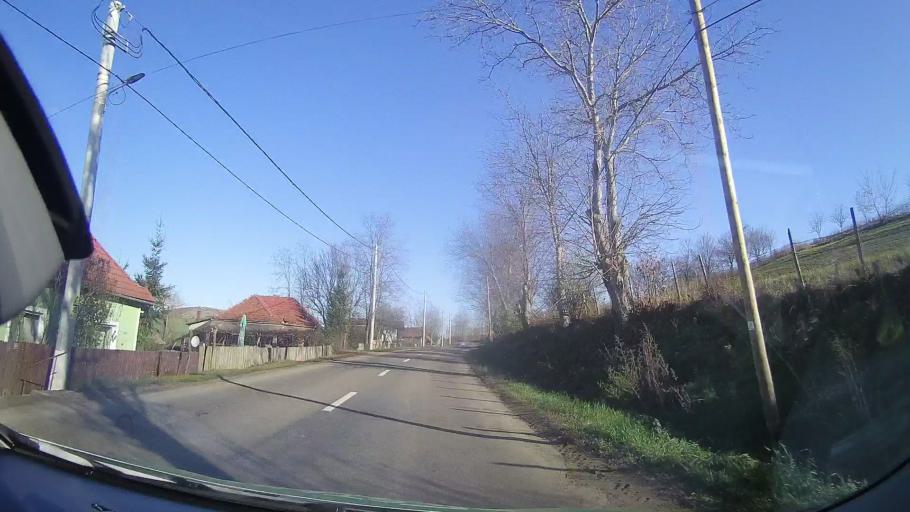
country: RO
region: Mures
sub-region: Comuna Band
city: Band
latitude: 46.5795
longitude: 24.3534
